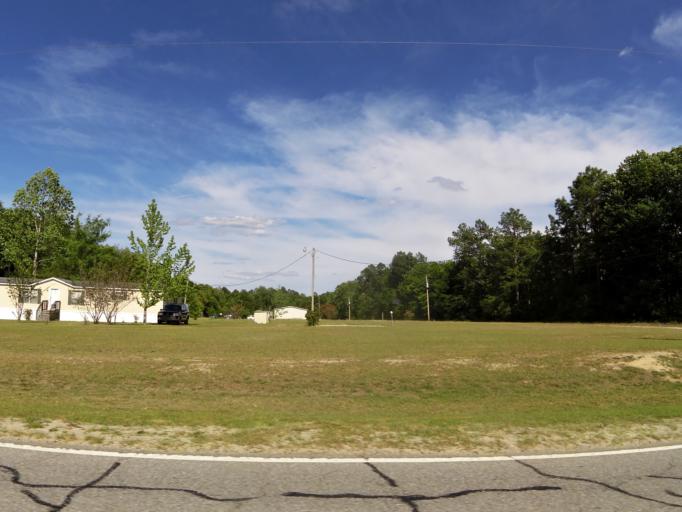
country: US
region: South Carolina
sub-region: Bamberg County
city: Denmark
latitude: 33.2129
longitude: -81.1749
